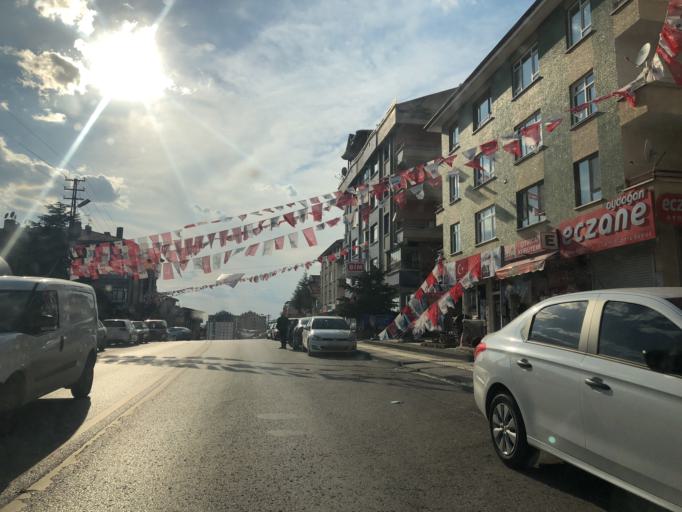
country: TR
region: Ankara
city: Ankara
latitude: 39.9843
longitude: 32.8451
